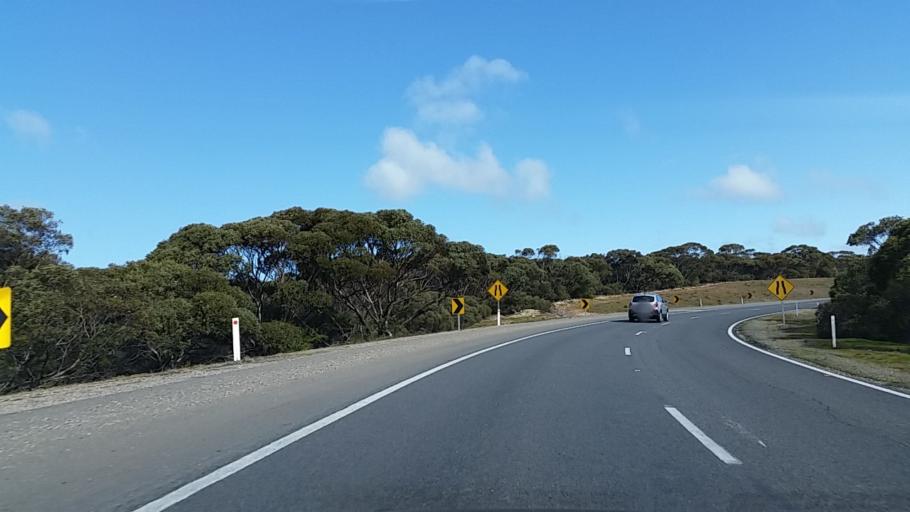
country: AU
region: South Australia
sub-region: Murray Bridge
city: Murray Bridge
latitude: -35.1453
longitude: 139.2275
